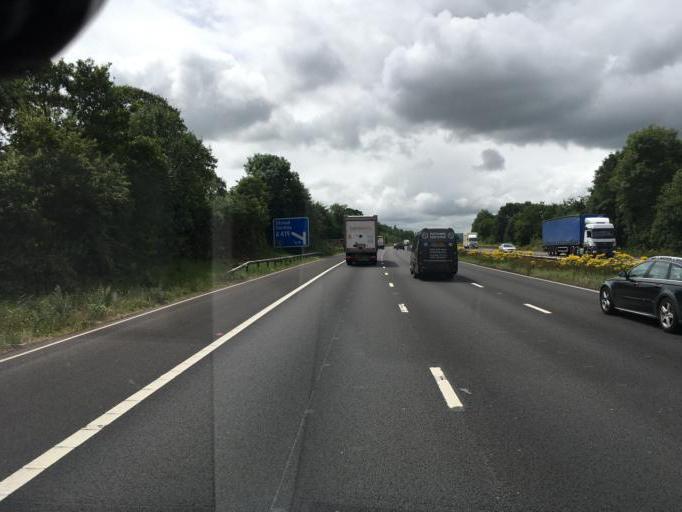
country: GB
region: England
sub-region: Gloucestershire
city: Stonehouse
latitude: 51.7707
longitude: -2.3118
